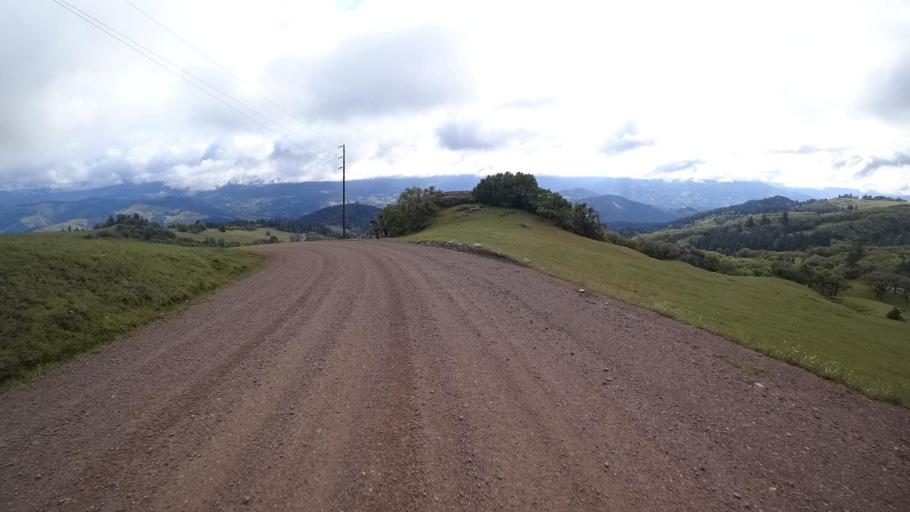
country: US
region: California
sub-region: Humboldt County
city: Redway
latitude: 40.2002
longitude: -123.6992
